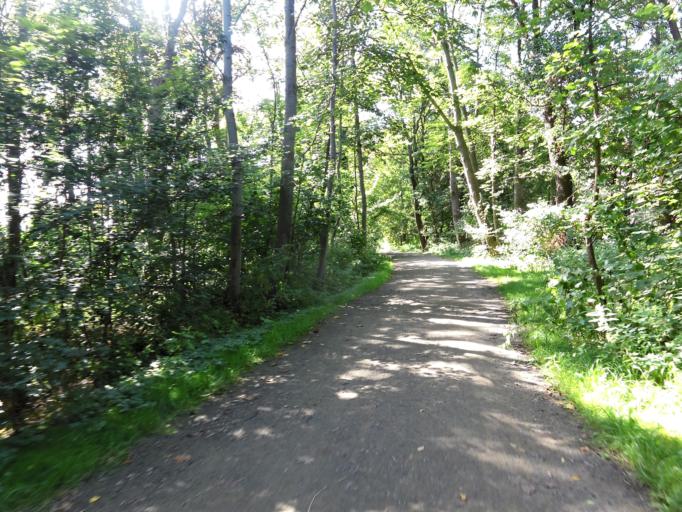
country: DE
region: Saxony
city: Leipzig
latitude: 51.3621
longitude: 12.4123
